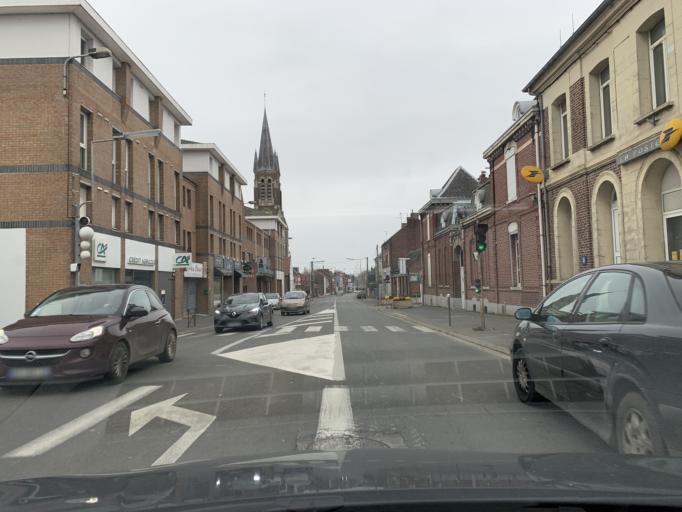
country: FR
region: Nord-Pas-de-Calais
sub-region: Departement du Nord
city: Neuville-Saint-Remy
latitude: 50.1877
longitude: 3.2220
